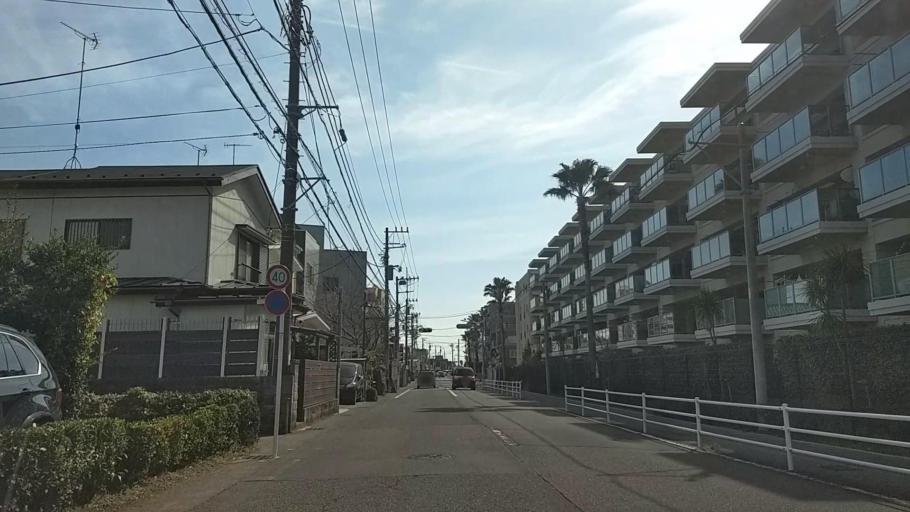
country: JP
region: Kanagawa
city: Fujisawa
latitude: 35.3222
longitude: 139.4540
